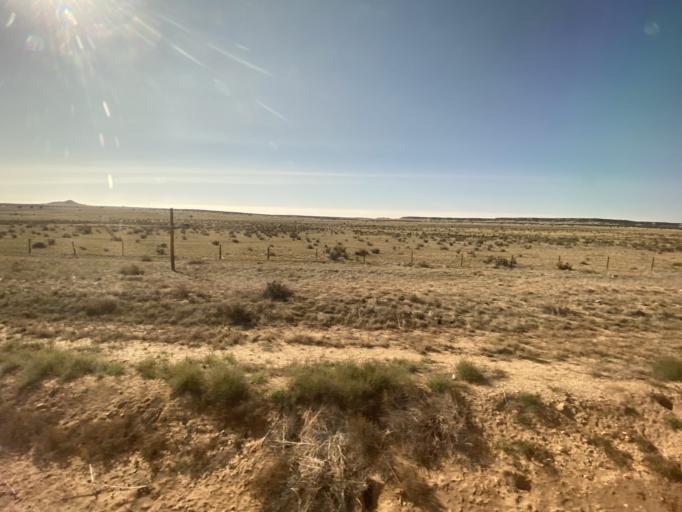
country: US
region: Colorado
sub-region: Otero County
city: Fowler
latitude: 37.5701
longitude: -104.0624
